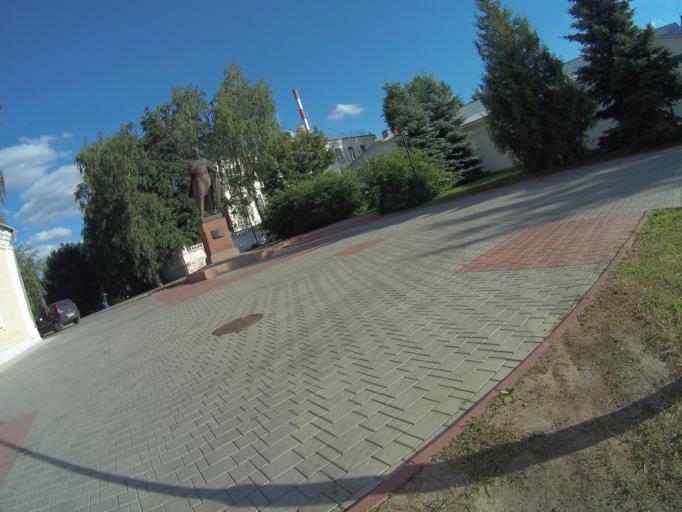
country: RU
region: Vladimir
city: Vladimir
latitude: 56.1306
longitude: 40.4115
